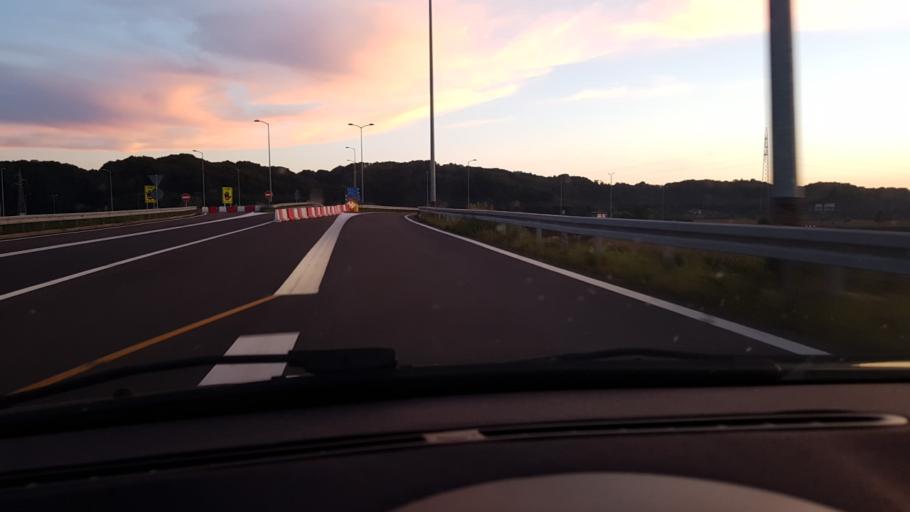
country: HR
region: Krapinsko-Zagorska
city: Selnica
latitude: 46.0390
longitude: 16.0764
